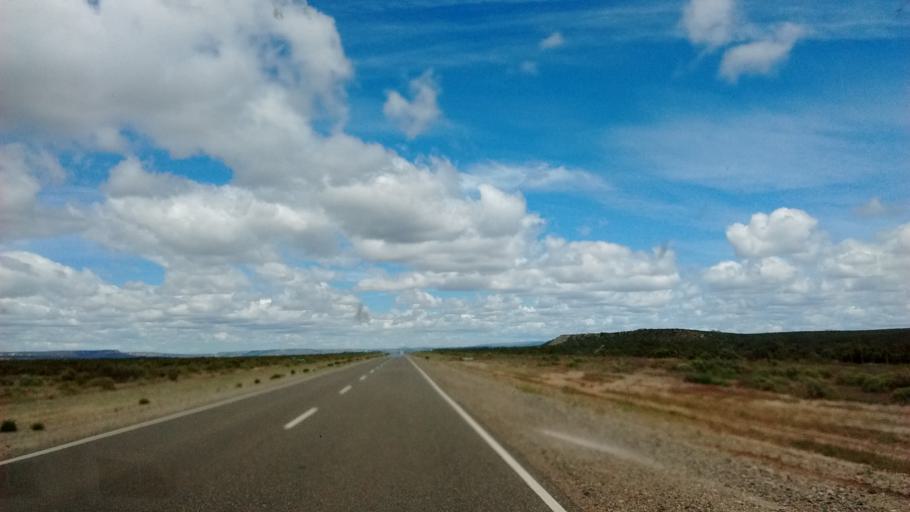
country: AR
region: Neuquen
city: Piedra del Aguila
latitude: -39.8397
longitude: -69.7750
